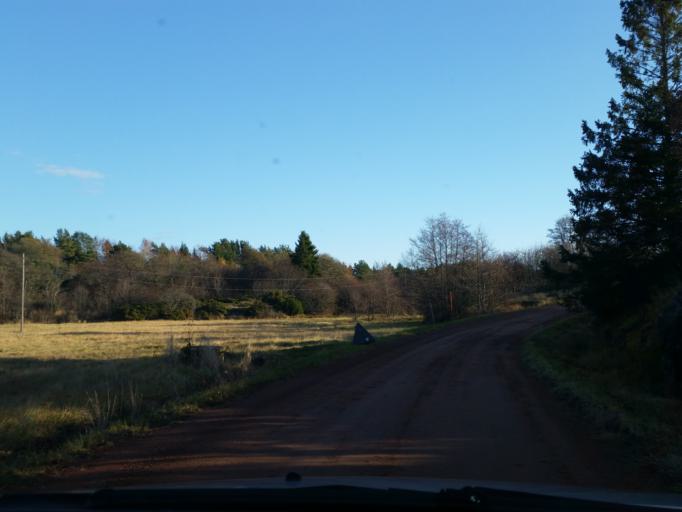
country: AX
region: Alands skaergard
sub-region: Braendoe
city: Braendoe
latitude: 60.4622
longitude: 21.0695
